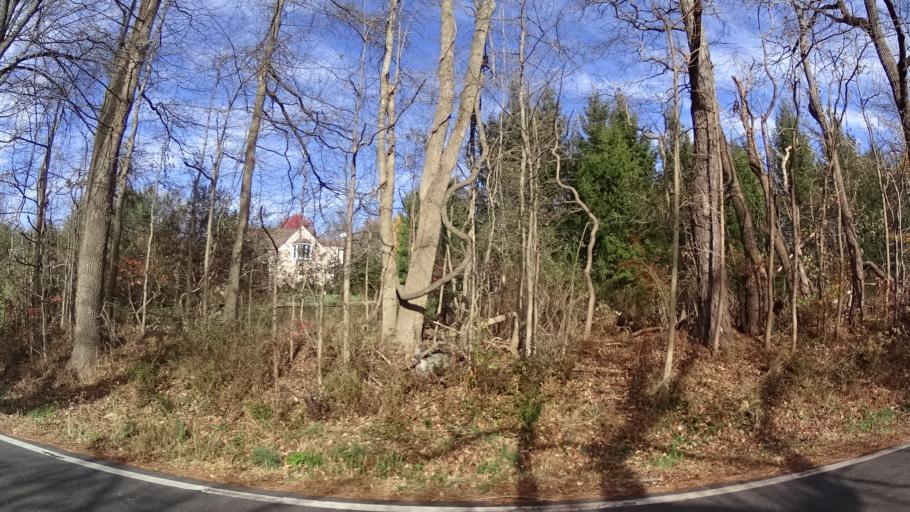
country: US
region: New Jersey
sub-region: Morris County
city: Mendham
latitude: 40.7793
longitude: -74.5834
